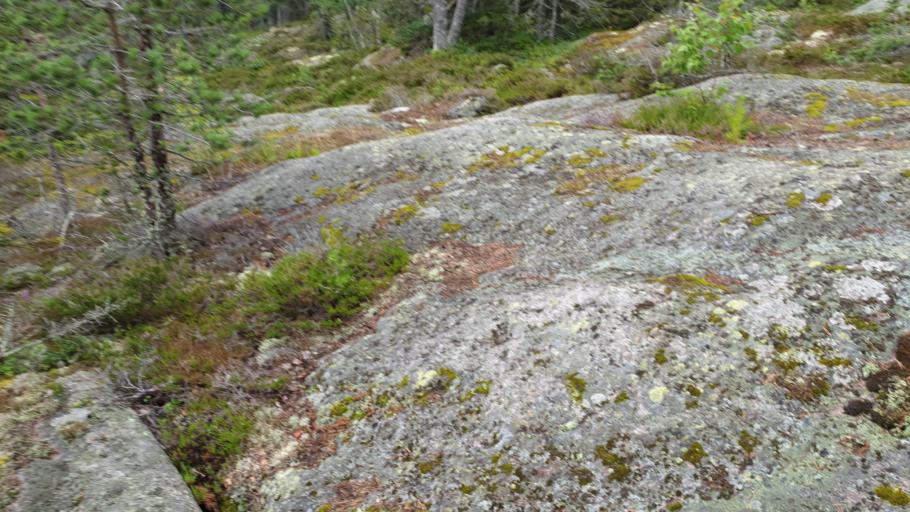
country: SE
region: Gaevleborg
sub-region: Hudiksvalls Kommun
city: Sorforsa
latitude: 61.6464
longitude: 16.7644
